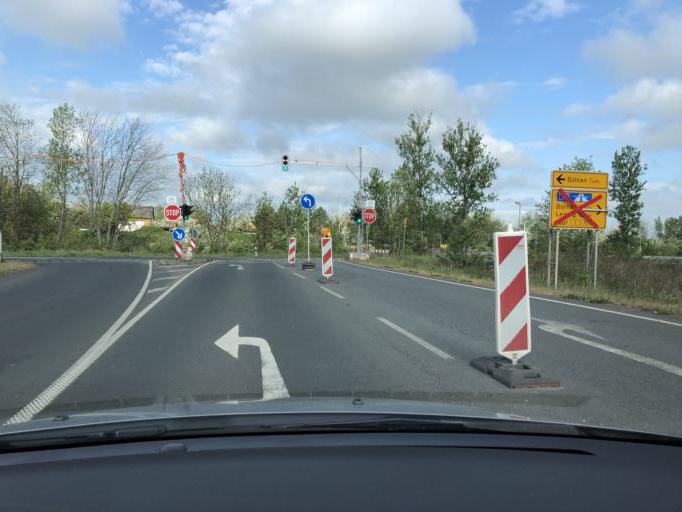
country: DE
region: Saxony
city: Bohlen
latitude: 51.2160
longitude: 12.3862
